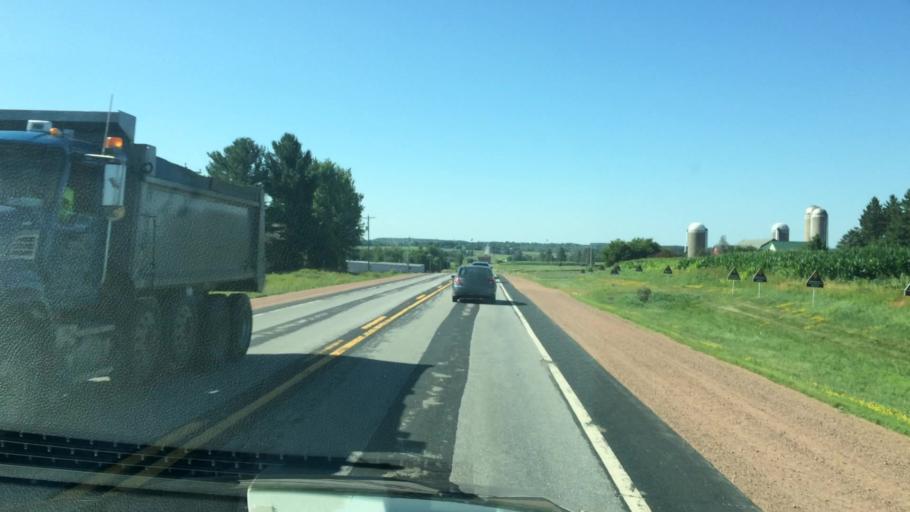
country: US
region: Wisconsin
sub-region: Marathon County
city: Stratford
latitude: 44.8345
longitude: -90.0792
